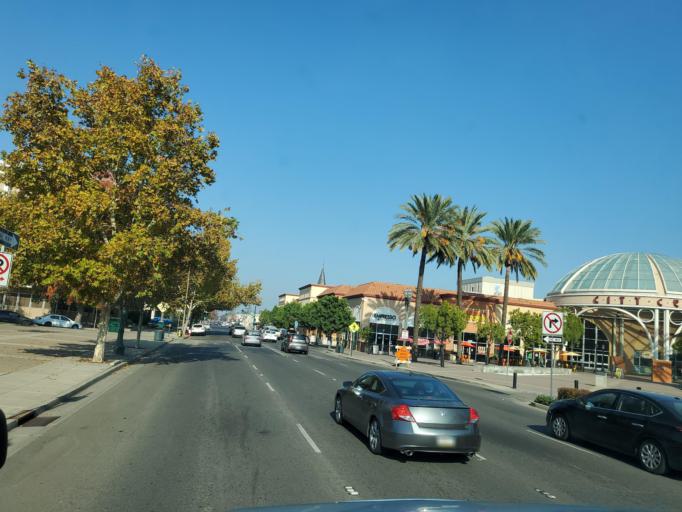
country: US
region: California
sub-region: San Joaquin County
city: Stockton
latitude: 37.9541
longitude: -121.2903
